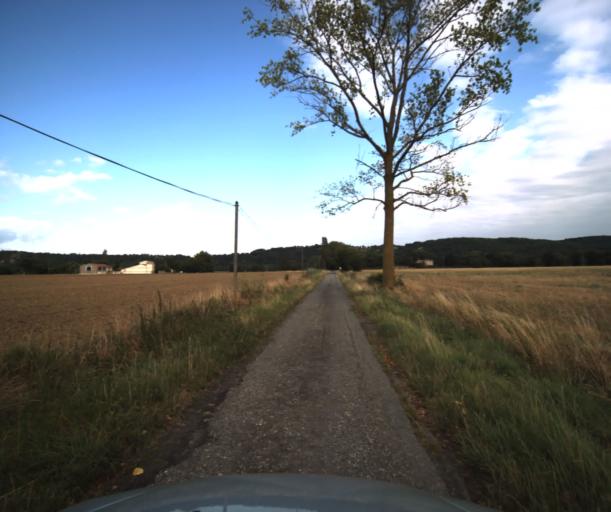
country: FR
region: Midi-Pyrenees
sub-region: Departement de la Haute-Garonne
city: Eaunes
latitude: 43.4377
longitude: 1.3132
